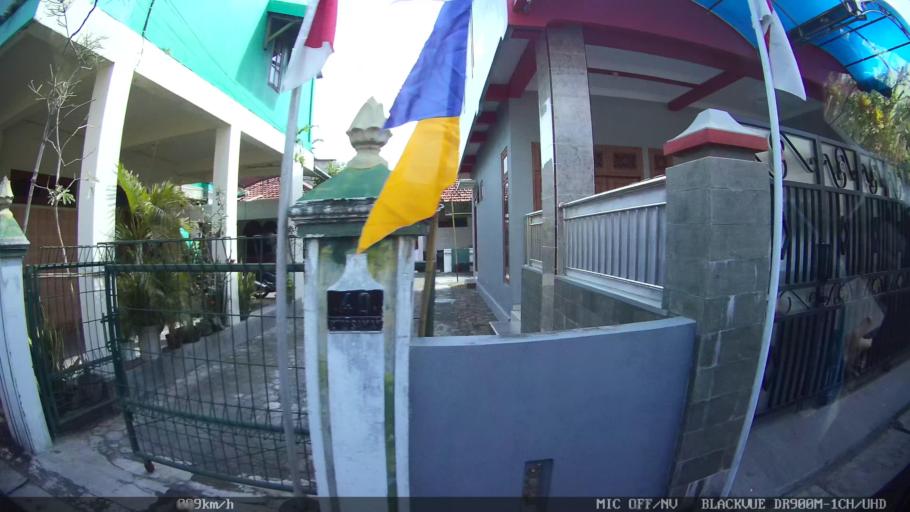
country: ID
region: Daerah Istimewa Yogyakarta
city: Kasihan
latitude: -7.8352
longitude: 110.3679
